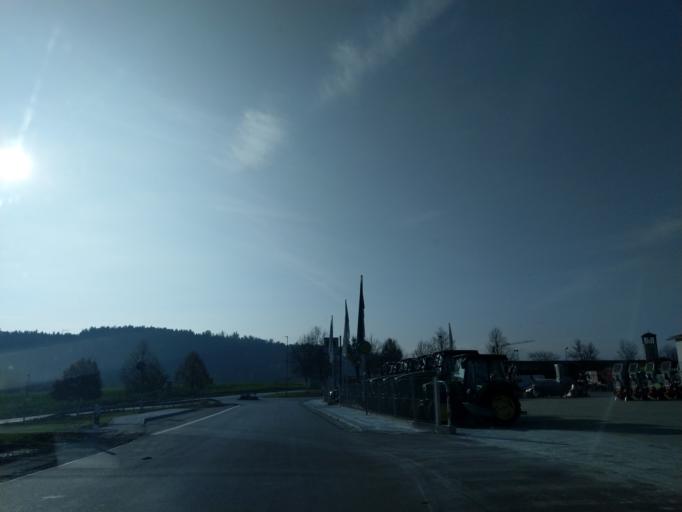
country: DE
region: Bavaria
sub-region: Lower Bavaria
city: Auerbach
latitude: 48.8033
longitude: 13.0927
